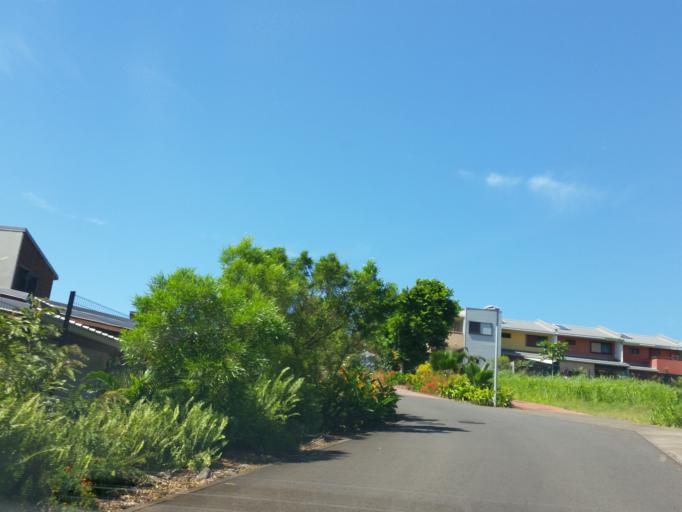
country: RE
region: Reunion
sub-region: Reunion
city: Sainte-Marie
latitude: -20.9148
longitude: 55.5199
